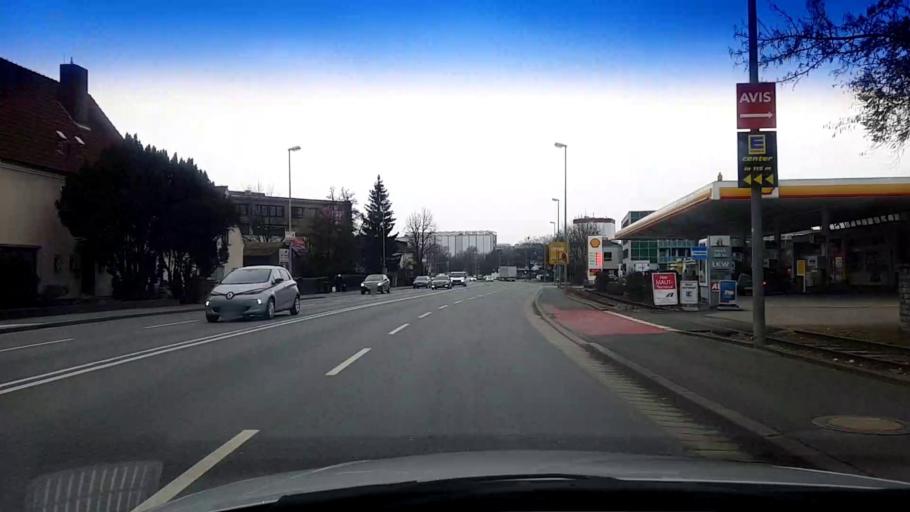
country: DE
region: Bavaria
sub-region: Upper Franconia
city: Kulmbach
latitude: 50.1011
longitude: 11.4424
